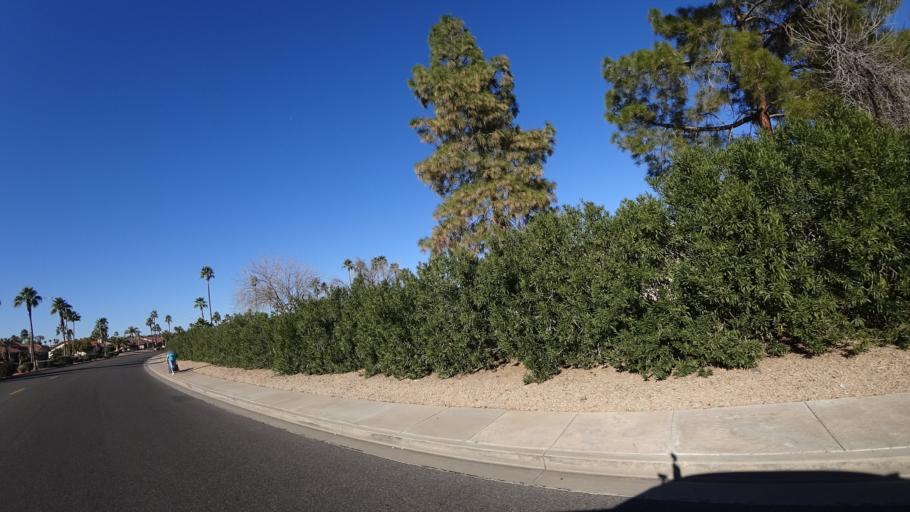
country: US
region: Arizona
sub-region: Maricopa County
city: Sun City West
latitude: 33.6729
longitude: -112.3536
